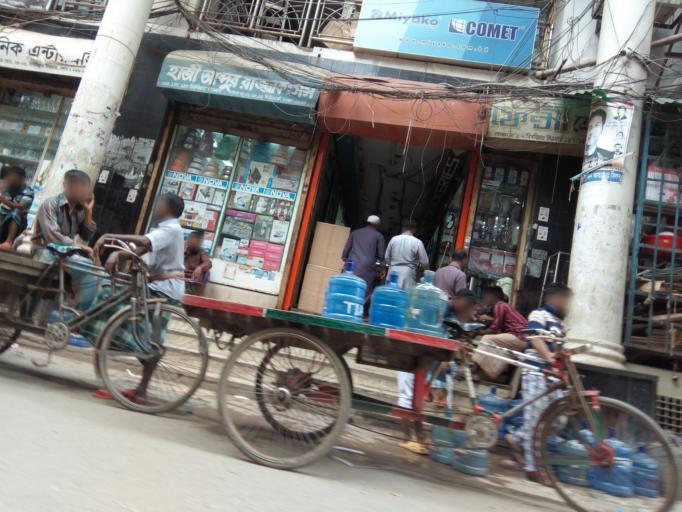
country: BD
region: Dhaka
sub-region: Dhaka
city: Dhaka
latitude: 23.7136
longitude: 90.3989
